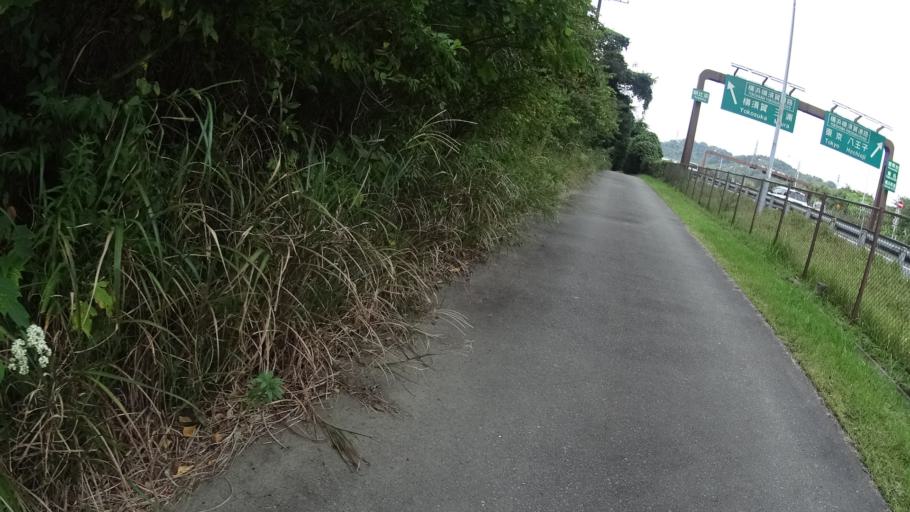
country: JP
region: Kanagawa
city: Zushi
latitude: 35.3545
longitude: 139.6016
